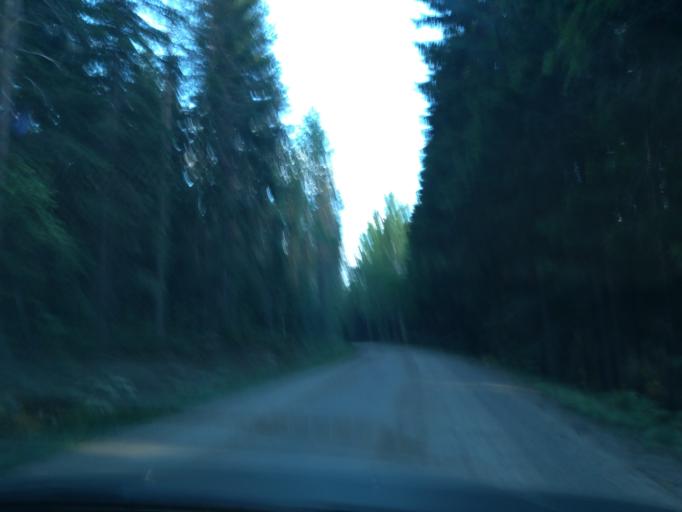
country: FI
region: Southern Savonia
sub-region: Mikkeli
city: Puumala
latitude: 61.6034
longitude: 28.1172
